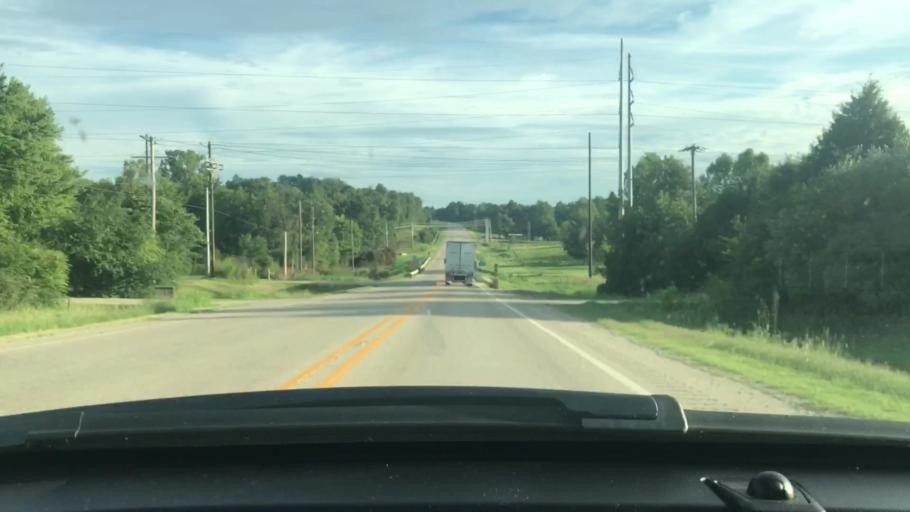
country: US
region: Arkansas
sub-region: Lawrence County
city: Hoxie
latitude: 36.1393
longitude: -91.1581
